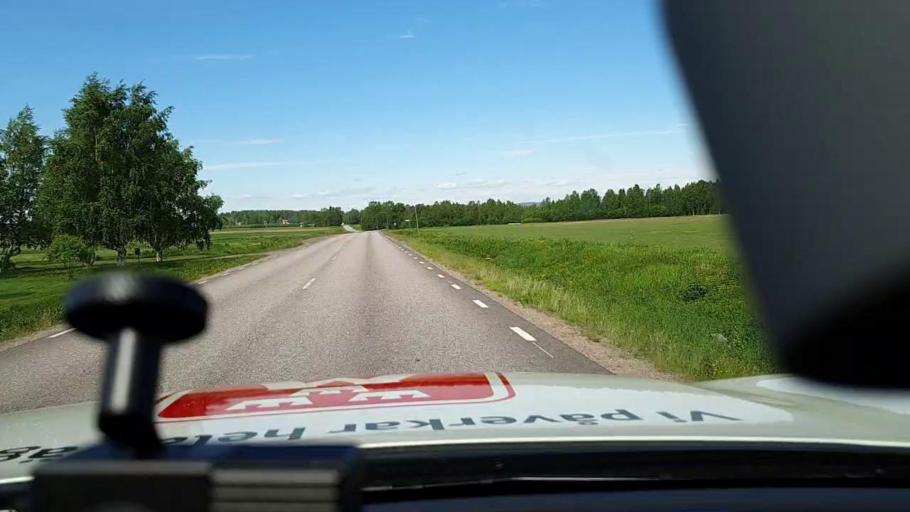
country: SE
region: Norrbotten
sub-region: Lulea Kommun
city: Sodra Sunderbyn
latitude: 65.6510
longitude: 21.8682
